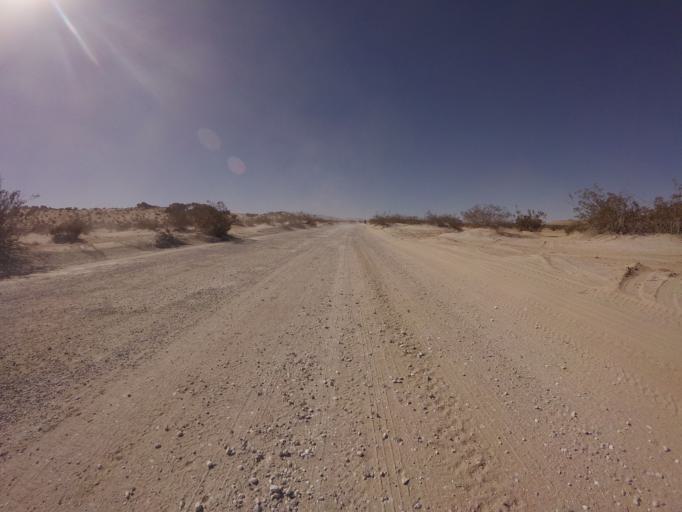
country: US
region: California
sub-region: San Bernardino County
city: Yucca Valley
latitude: 34.3896
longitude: -116.5294
